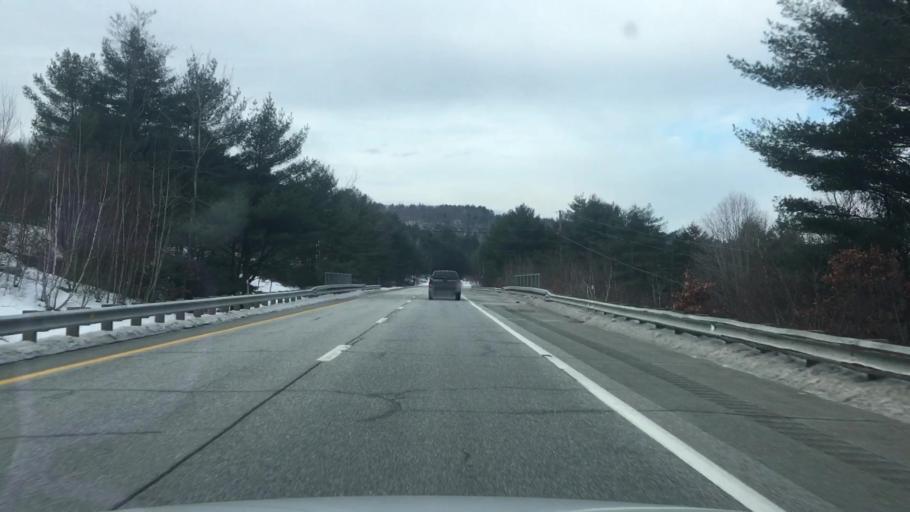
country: US
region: New Hampshire
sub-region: Merrimack County
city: Henniker
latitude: 43.2782
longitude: -71.8208
